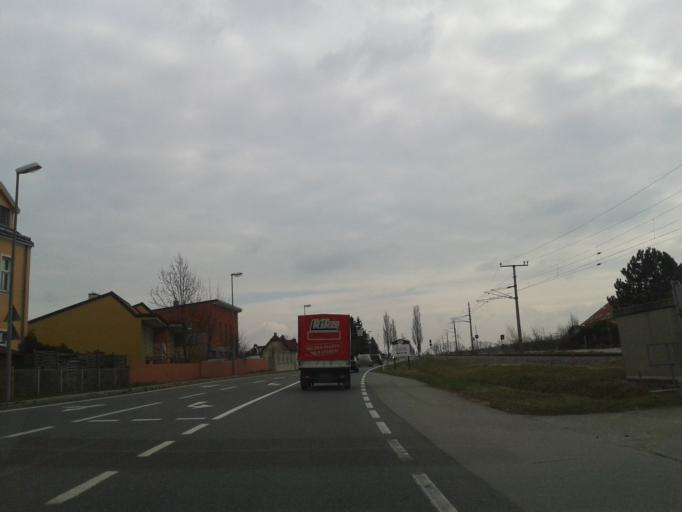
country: AT
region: Lower Austria
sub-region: Politischer Bezirk Ganserndorf
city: Orth an der Donau
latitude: 48.1109
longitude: 16.6920
